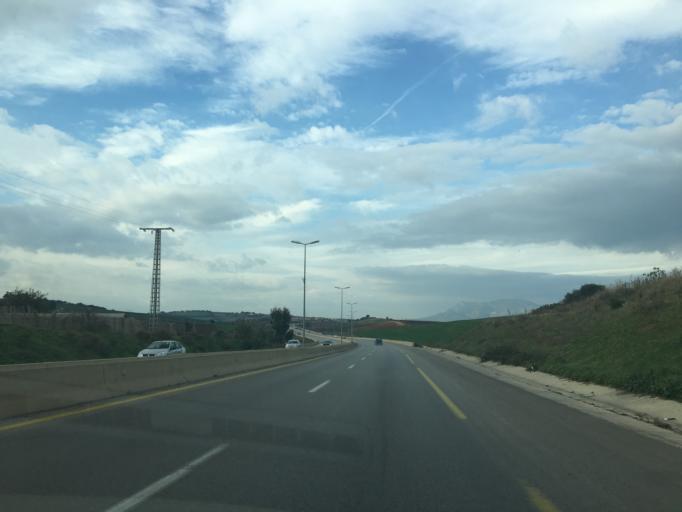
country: DZ
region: Tipaza
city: Tipasa
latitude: 36.5760
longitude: 2.5354
